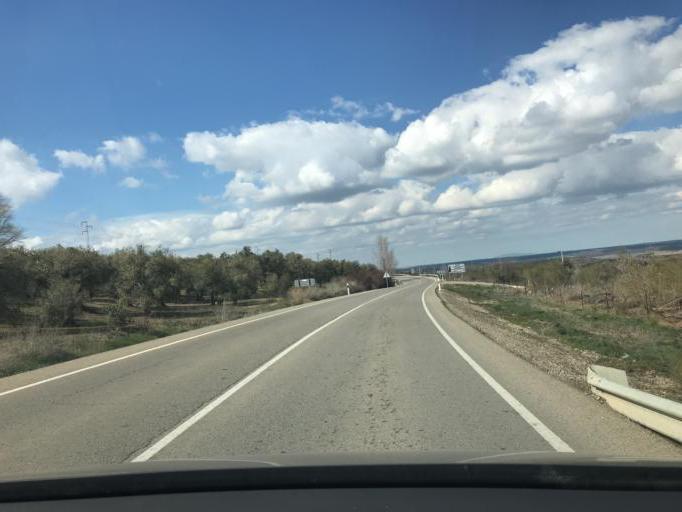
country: ES
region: Andalusia
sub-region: Provincia de Sevilla
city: Guadalcanal
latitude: 38.1144
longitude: -5.8237
